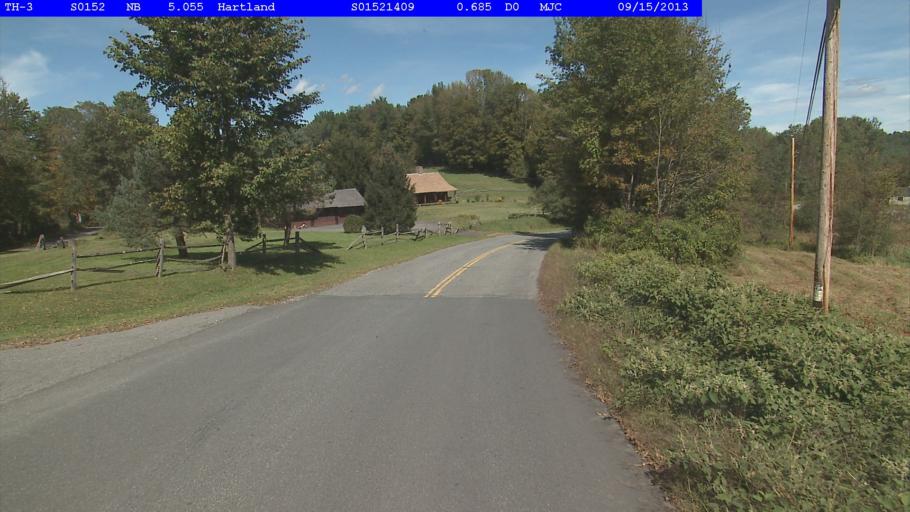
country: US
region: Vermont
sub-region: Windsor County
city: Windsor
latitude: 43.5324
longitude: -72.4378
